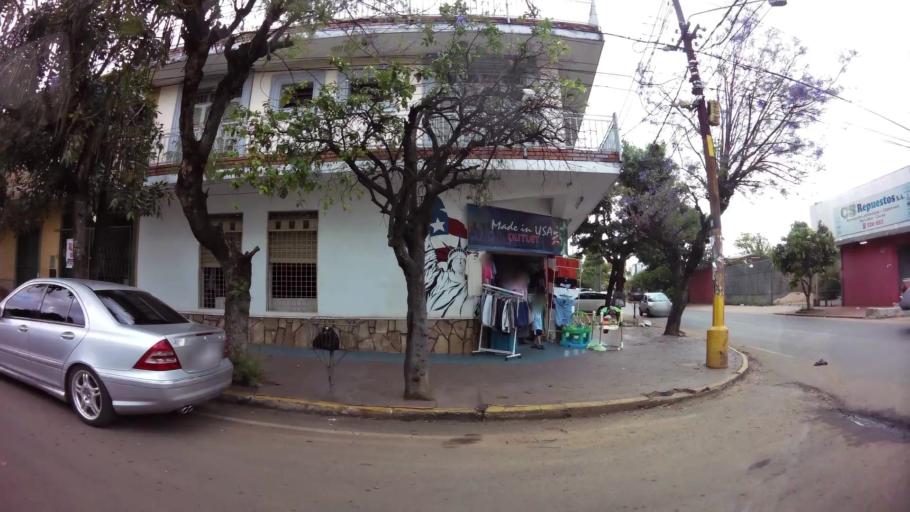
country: PY
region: Central
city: Fernando de la Mora
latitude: -25.3278
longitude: -57.5530
